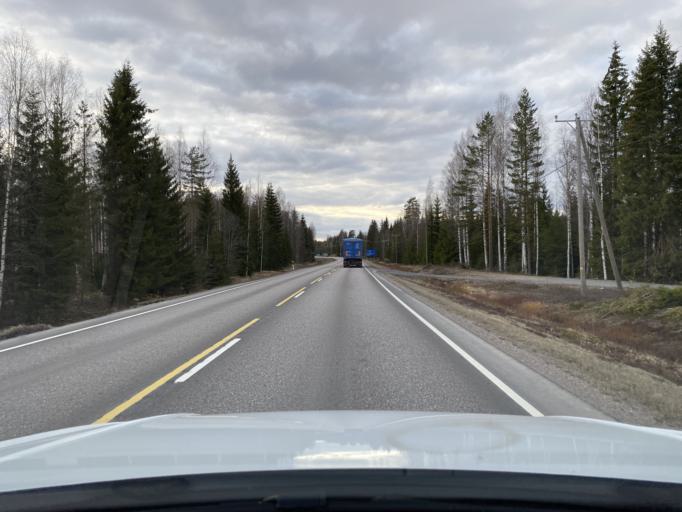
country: FI
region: Uusimaa
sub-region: Helsinki
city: Kaerkoelae
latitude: 60.8242
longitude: 24.0253
